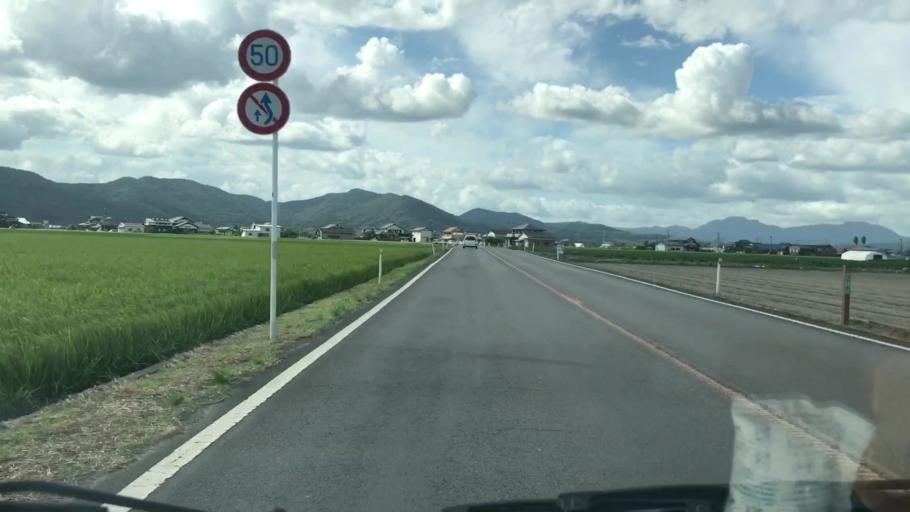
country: JP
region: Saga Prefecture
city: Kashima
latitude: 33.1372
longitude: 130.1391
